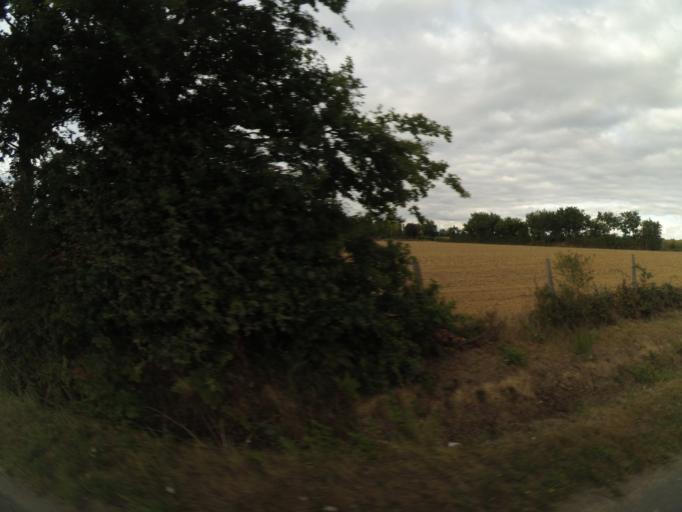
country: FR
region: Pays de la Loire
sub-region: Departement de la Vendee
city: Saint-Andre-Treize-Voies
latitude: 46.9260
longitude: -1.3987
